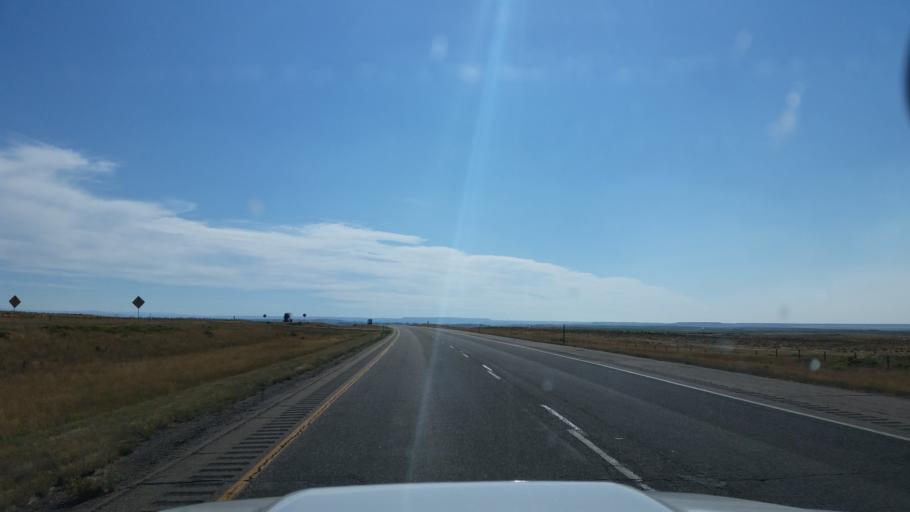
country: US
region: Wyoming
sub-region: Uinta County
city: Lyman
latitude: 41.3838
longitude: -110.2240
